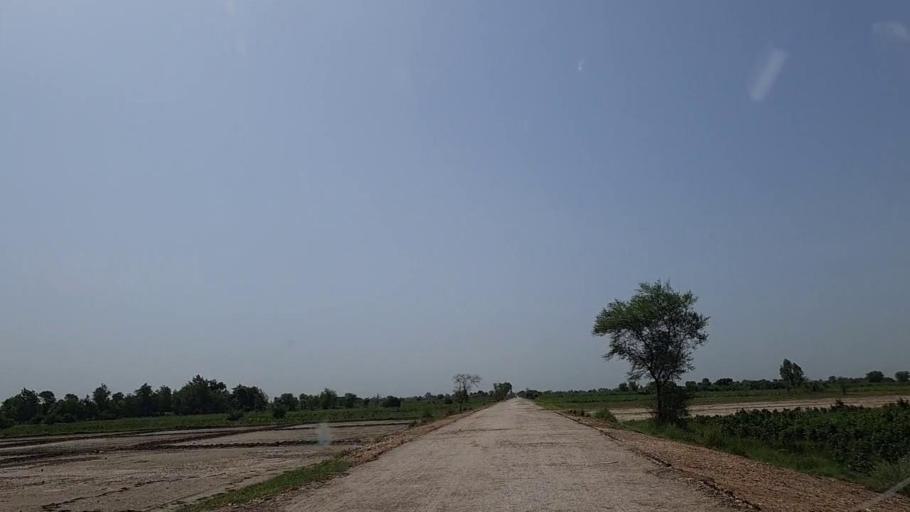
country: PK
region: Sindh
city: Naushahro Firoz
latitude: 26.8571
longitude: 68.0066
